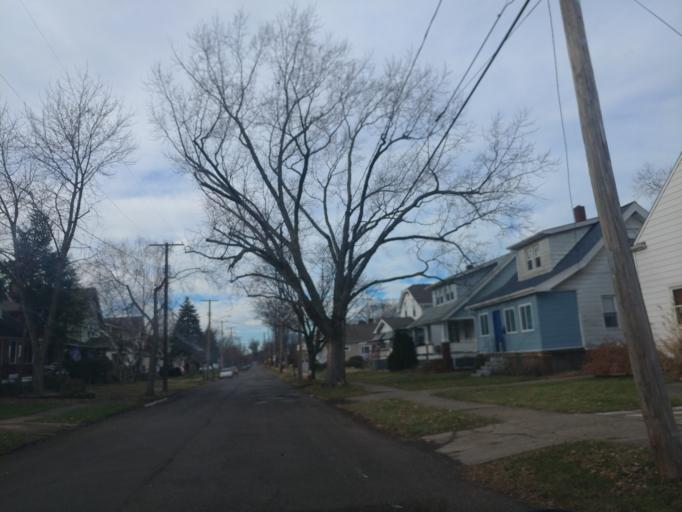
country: US
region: Ohio
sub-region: Cuyahoga County
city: Brooklyn
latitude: 41.4290
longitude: -81.7187
